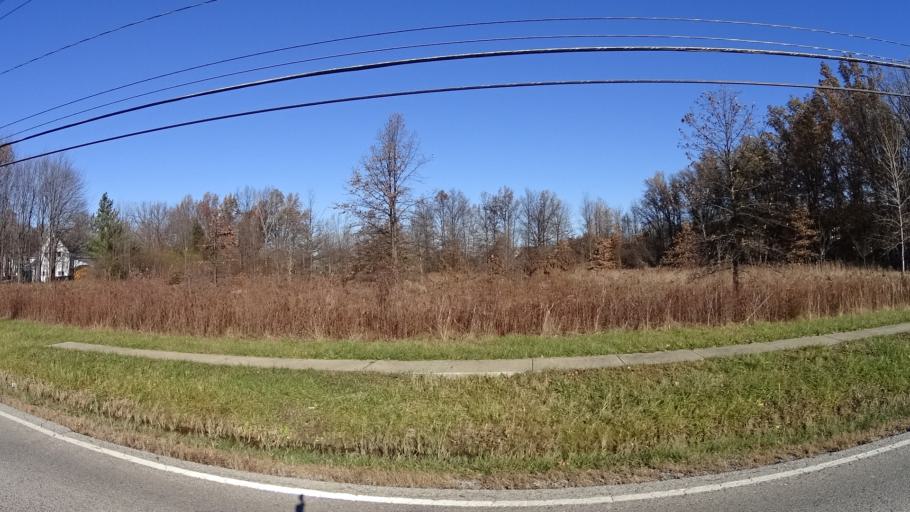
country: US
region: Ohio
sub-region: Lorain County
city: Avon Center
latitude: 41.4782
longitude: -81.9819
